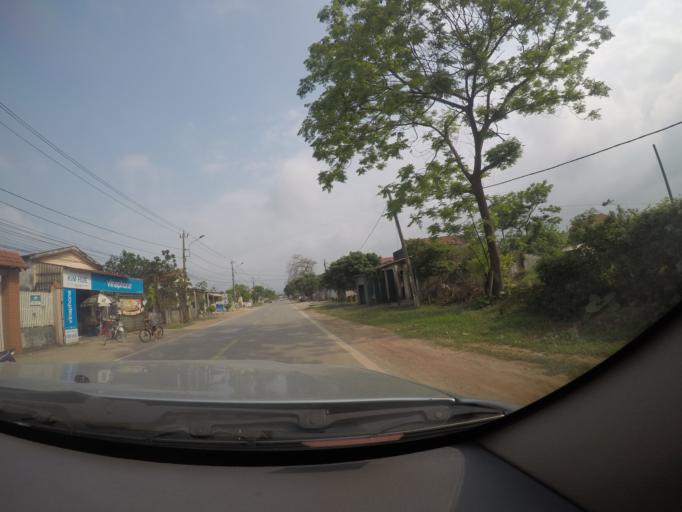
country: VN
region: Quang Binh
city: Kwang Binh
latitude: 17.4579
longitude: 106.5650
